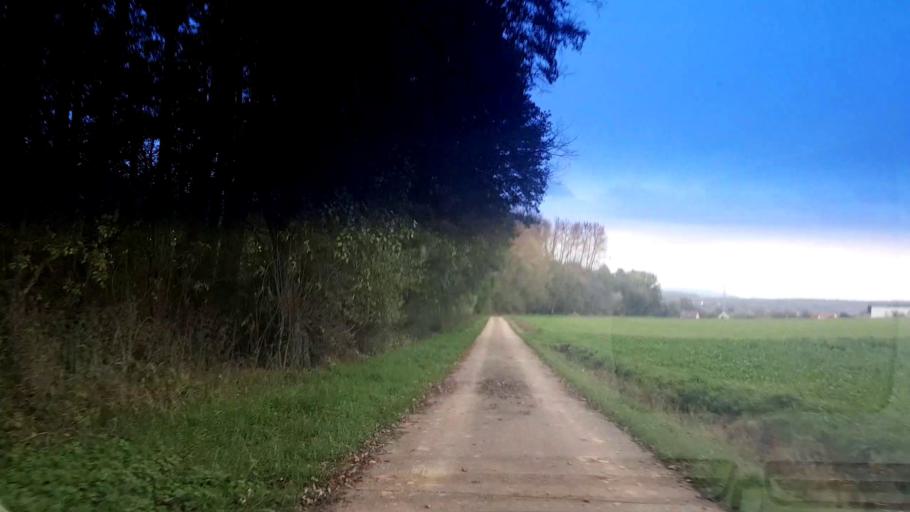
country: DE
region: Bavaria
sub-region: Upper Franconia
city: Memmelsdorf
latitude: 49.9653
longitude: 10.9581
